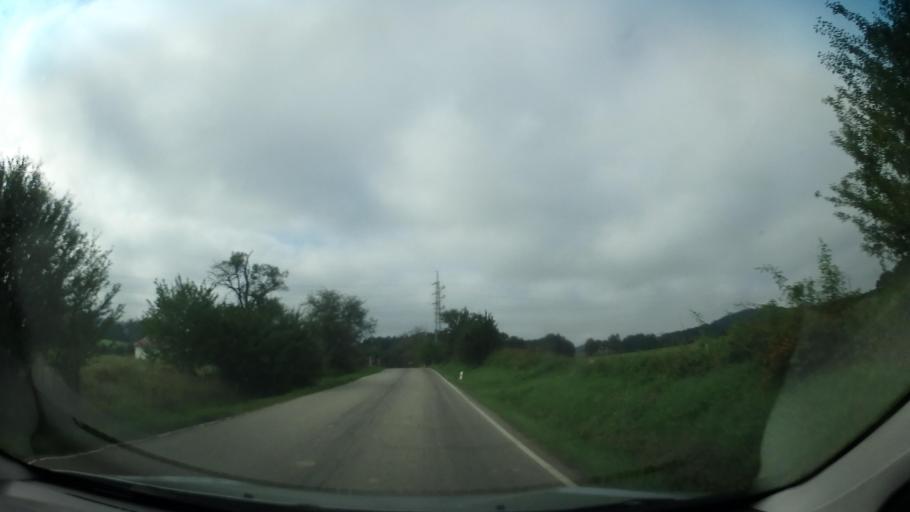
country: CZ
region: Central Bohemia
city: Neveklov
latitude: 49.7488
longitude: 14.5200
